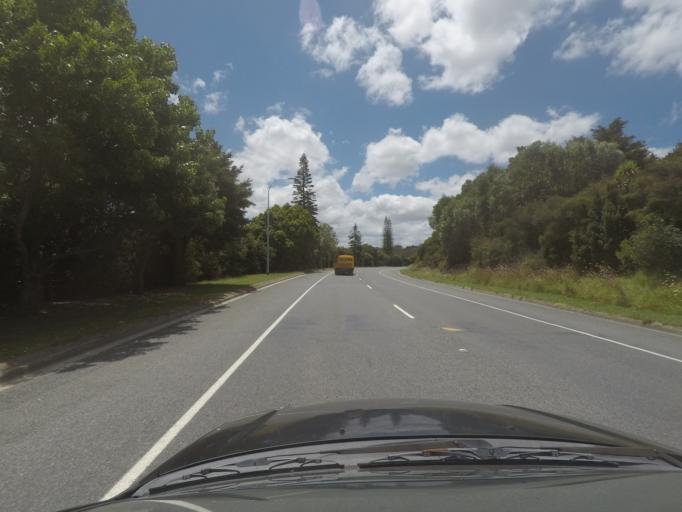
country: NZ
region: Northland
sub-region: Whangarei
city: Whangarei
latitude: -35.7477
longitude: 174.3208
